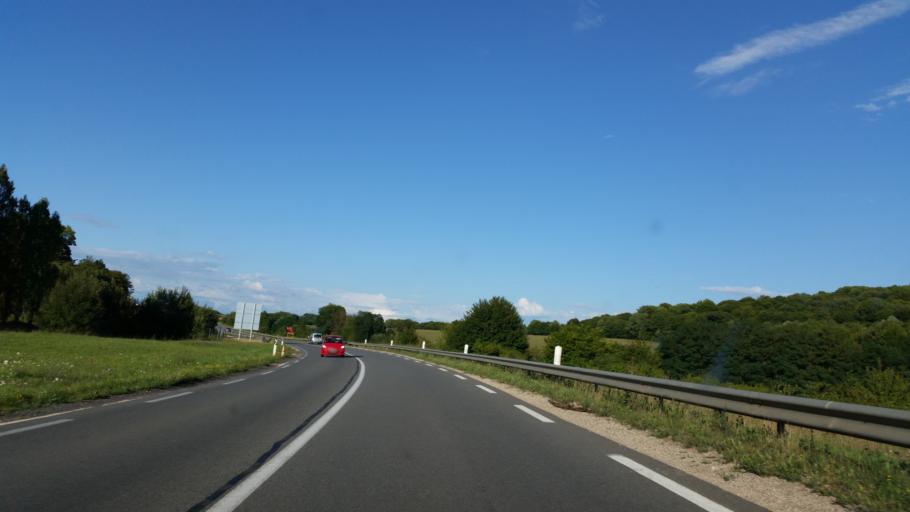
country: FR
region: Franche-Comte
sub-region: Departement de la Haute-Saone
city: Hericourt
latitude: 47.5910
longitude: 6.7963
